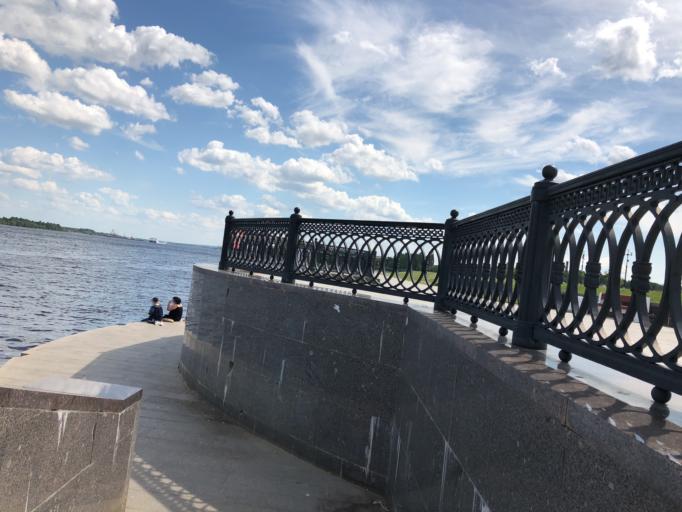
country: RU
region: Jaroslavl
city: Yaroslavl
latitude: 57.6188
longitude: 39.9058
